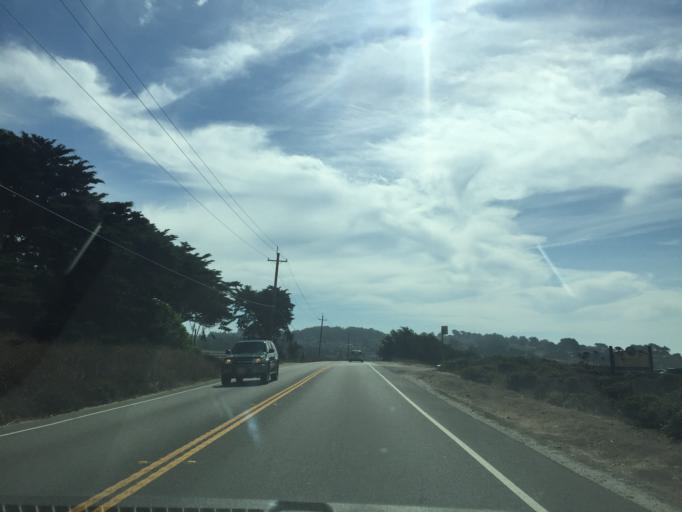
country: US
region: California
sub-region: San Mateo County
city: Montara
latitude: 37.5525
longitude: -122.5123
